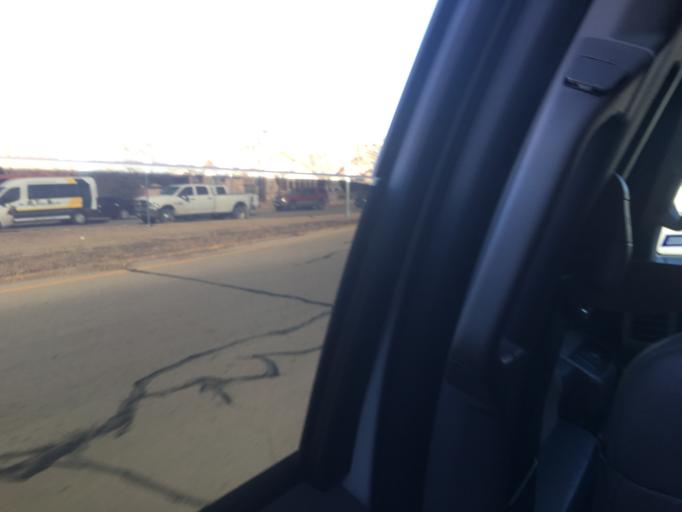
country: US
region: Texas
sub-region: Parker County
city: Weatherford
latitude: 32.7584
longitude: -97.8141
